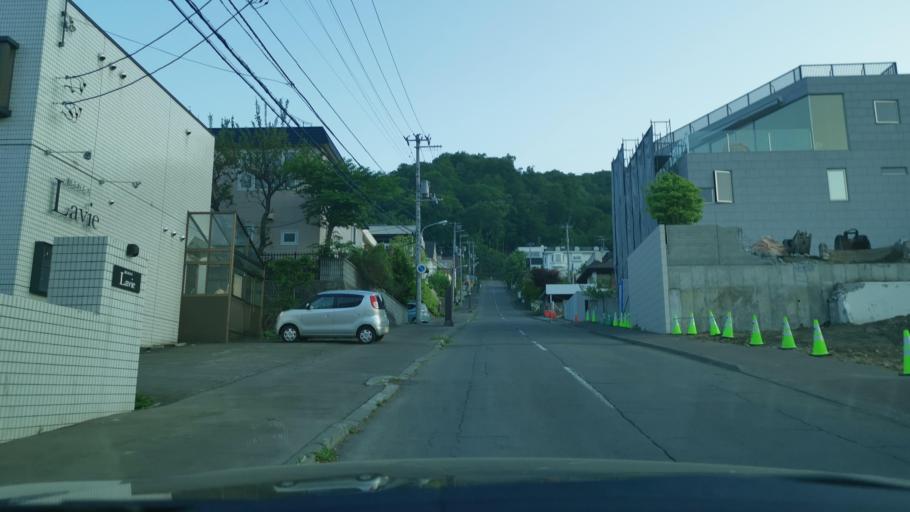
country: JP
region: Hokkaido
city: Sapporo
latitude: 43.0361
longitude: 141.3156
